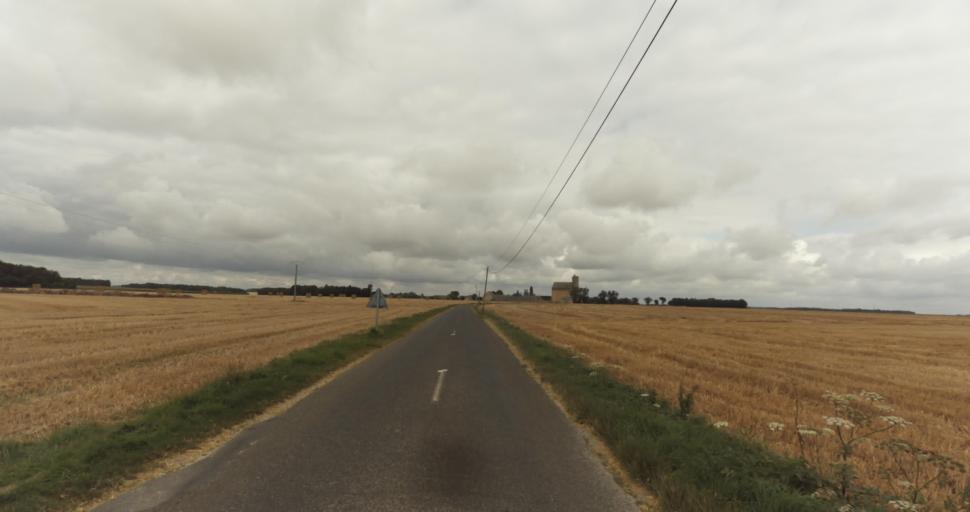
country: FR
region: Haute-Normandie
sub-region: Departement de l'Eure
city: La Couture-Boussey
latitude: 48.9405
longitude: 1.3216
